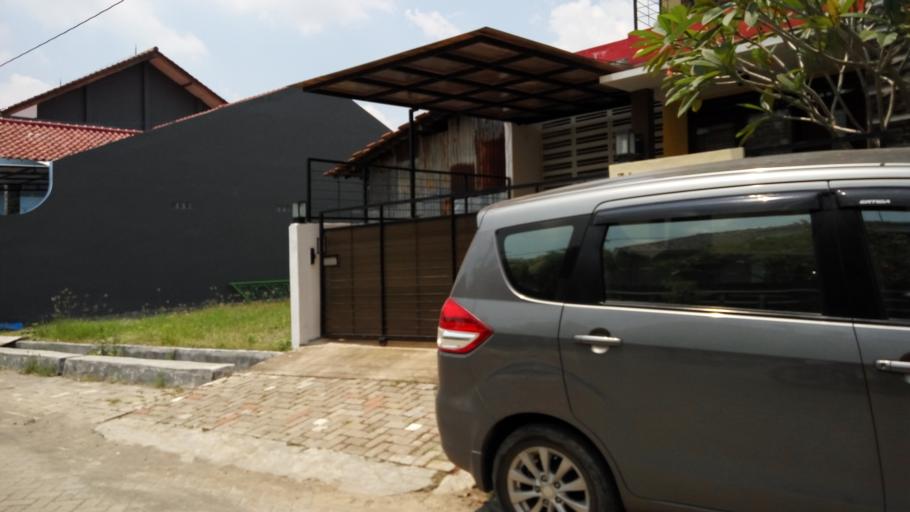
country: ID
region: Central Java
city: Mranggen
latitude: -7.0433
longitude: 110.4746
